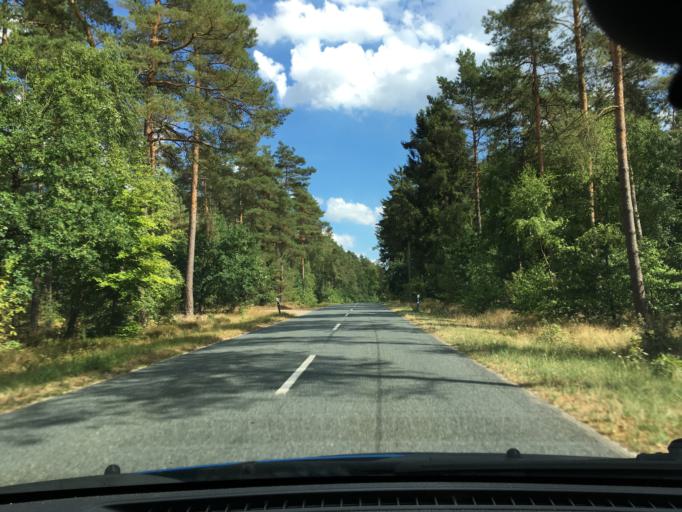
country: DE
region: Lower Saxony
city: Rehlingen
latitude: 53.0827
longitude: 10.2172
